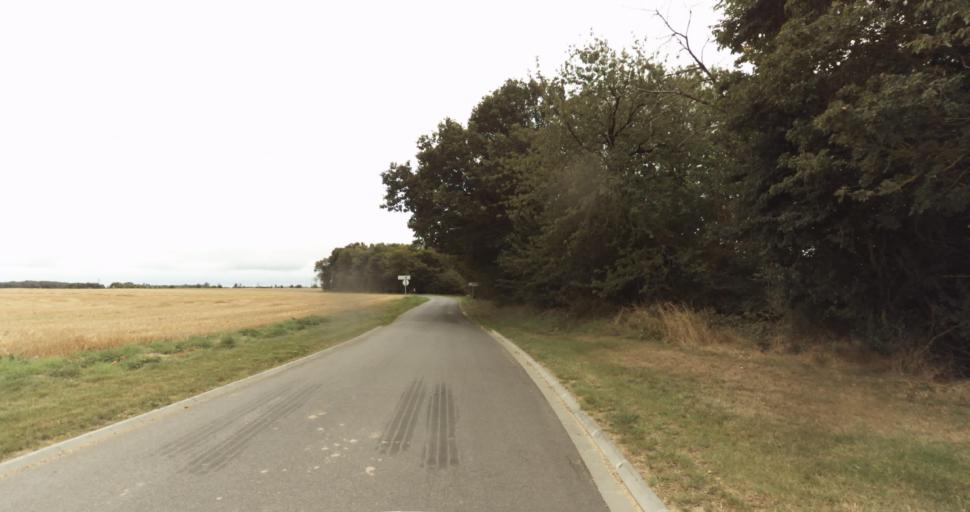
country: FR
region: Haute-Normandie
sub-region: Departement de l'Eure
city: Evreux
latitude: 48.9205
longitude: 1.1887
